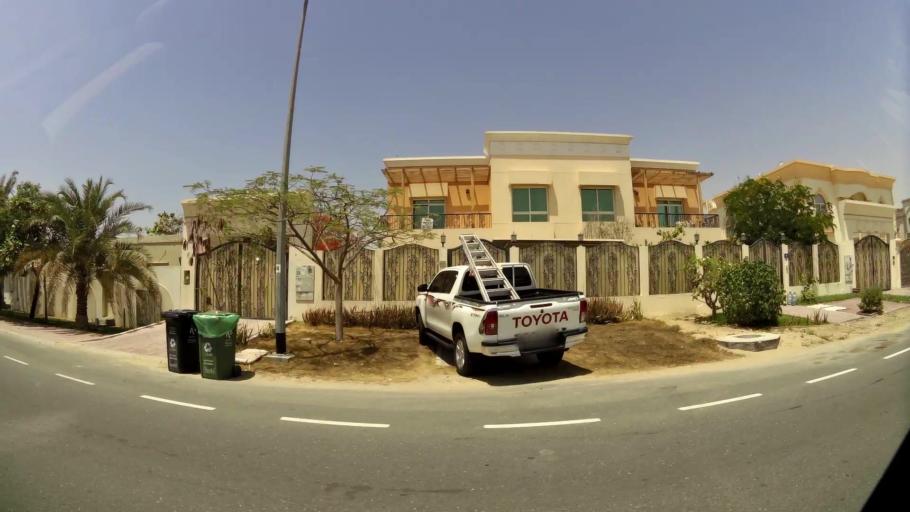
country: AE
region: Dubai
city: Dubai
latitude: 25.0922
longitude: 55.2051
